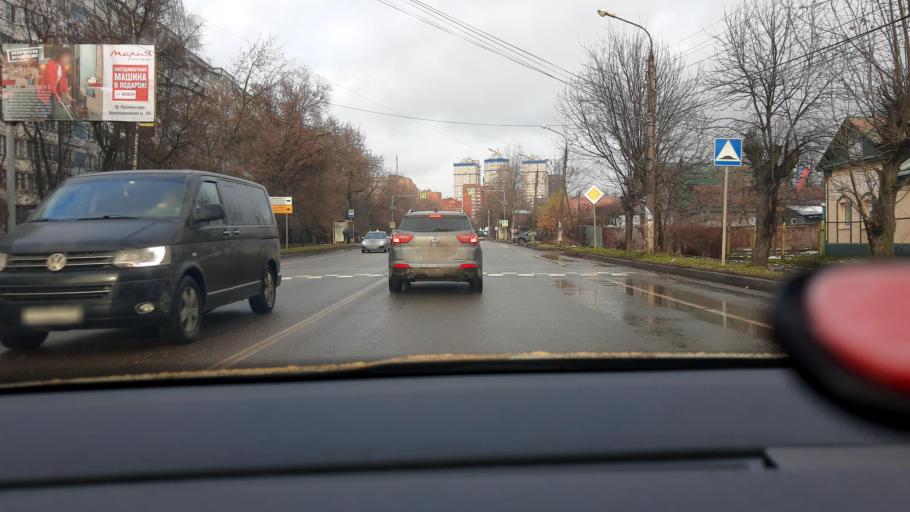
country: RU
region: Moskovskaya
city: Pushkino
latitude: 55.9927
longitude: 37.8672
